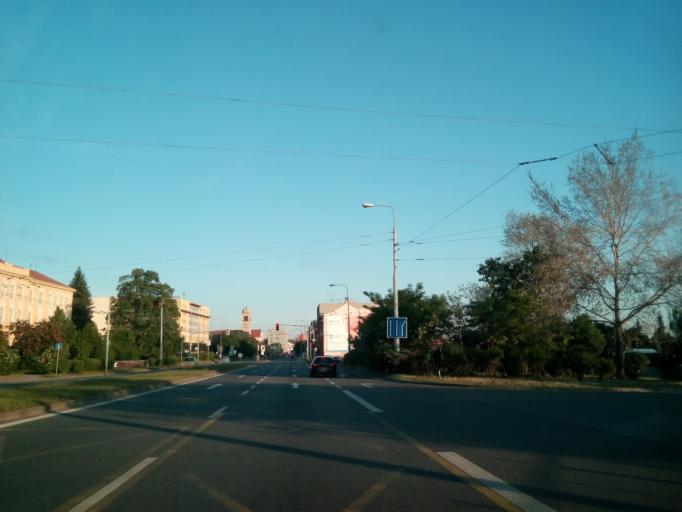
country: CZ
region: South Moravian
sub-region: Mesto Brno
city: Brno
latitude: 49.2029
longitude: 16.6423
